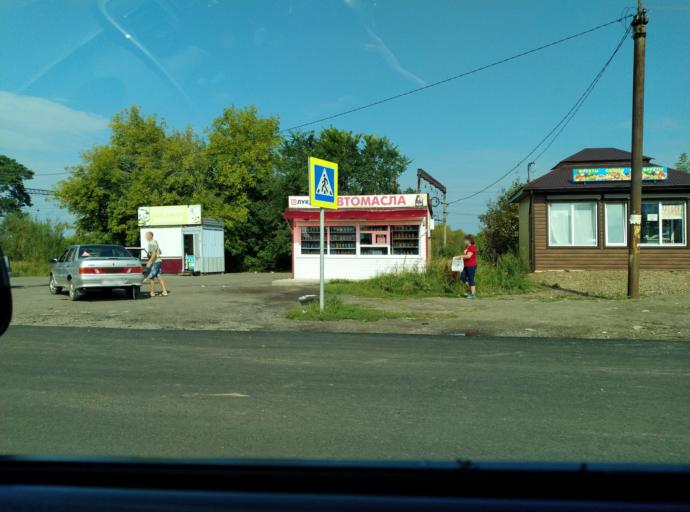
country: RU
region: Tomsk
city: Bogashevo
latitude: 56.3664
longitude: 85.1468
